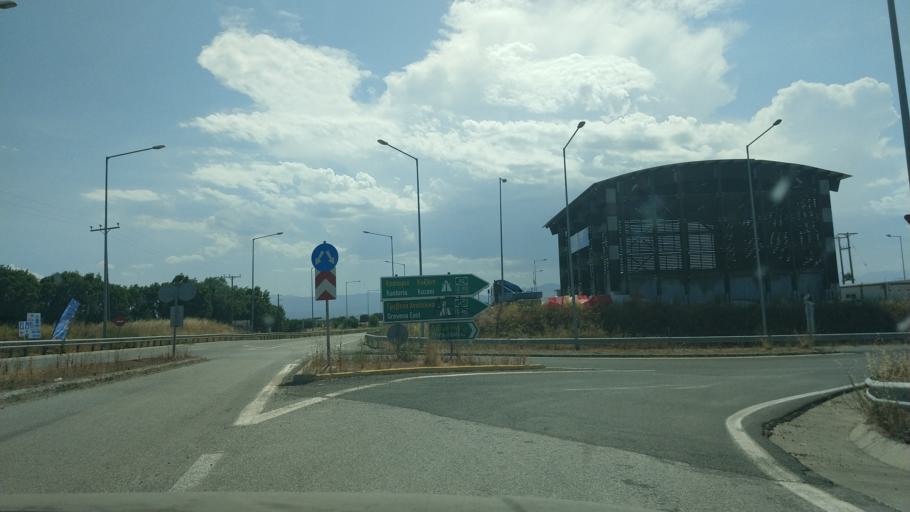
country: GR
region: West Macedonia
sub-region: Nomos Grevenon
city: Grevena
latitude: 40.0653
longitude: 21.4406
